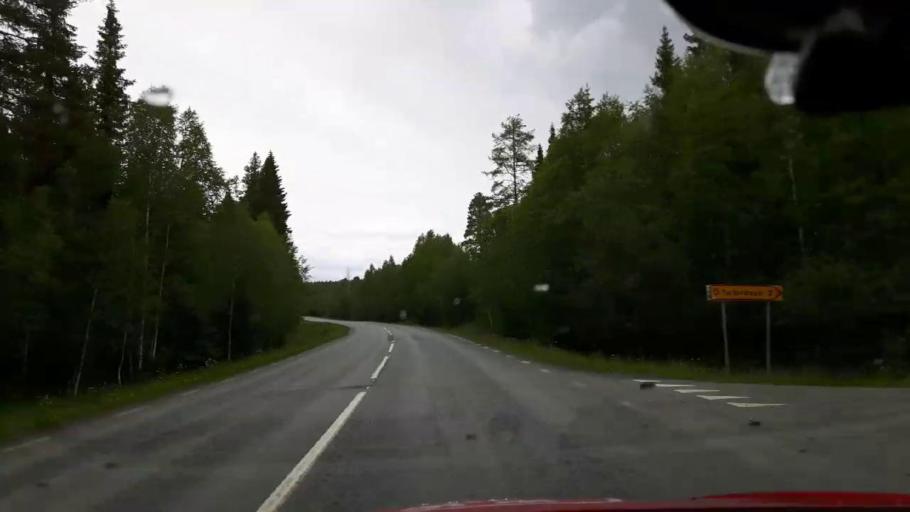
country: SE
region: Jaemtland
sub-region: Krokoms Kommun
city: Krokom
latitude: 63.4329
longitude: 14.2078
